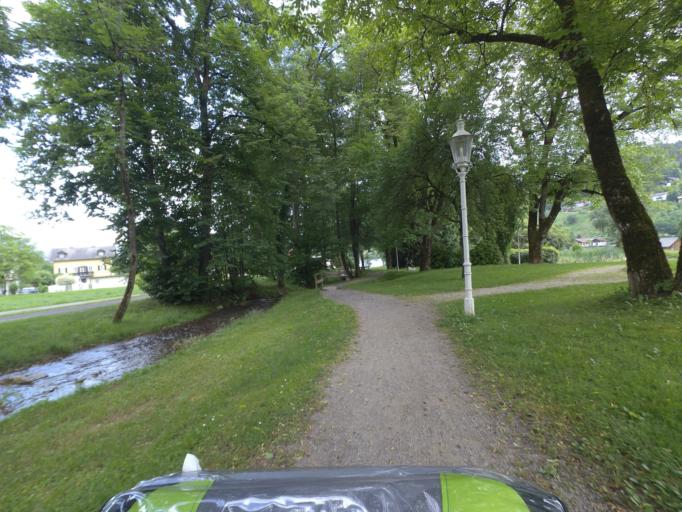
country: AT
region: Carinthia
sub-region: Politischer Bezirk Spittal an der Drau
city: Seeboden
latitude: 46.8147
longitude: 13.5135
